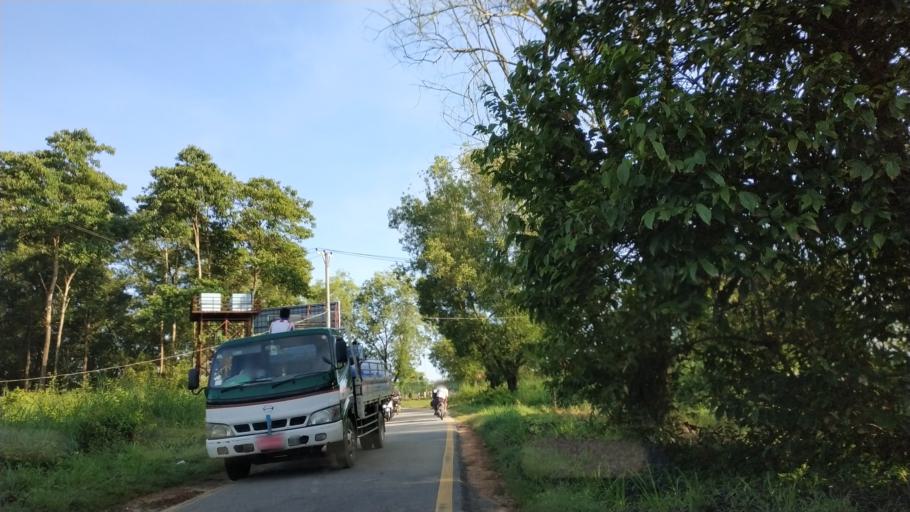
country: MM
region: Tanintharyi
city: Dawei
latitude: 14.0988
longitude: 98.2028
